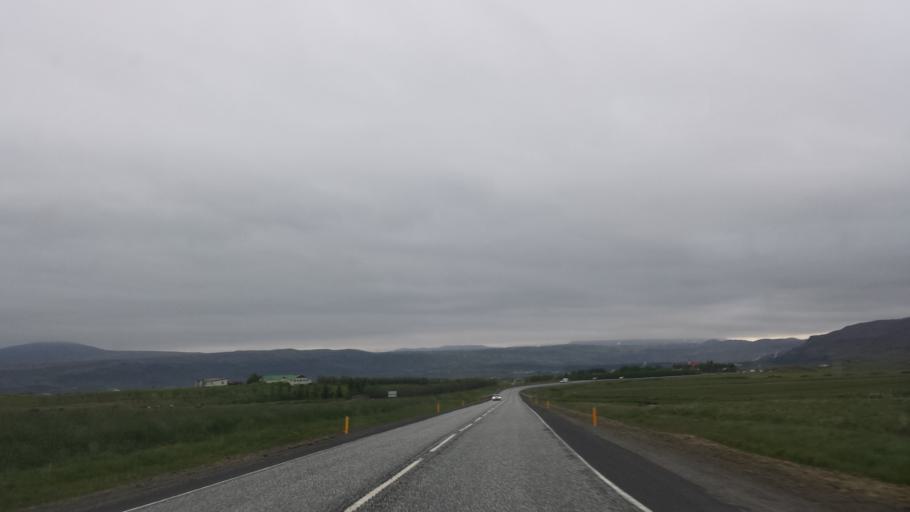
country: IS
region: South
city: Hveragerdi
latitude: 63.9630
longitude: -21.1287
